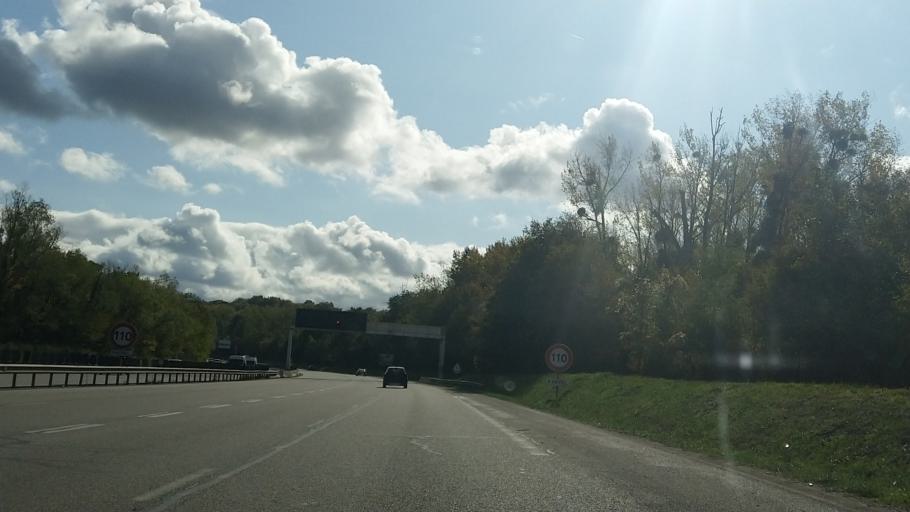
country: FR
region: Ile-de-France
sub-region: Departement du Val-d'Oise
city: Mours
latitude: 49.1208
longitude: 2.2526
